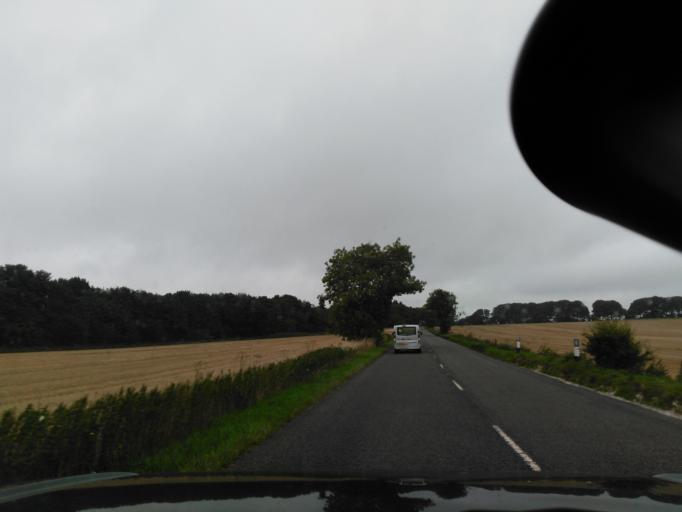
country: GB
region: England
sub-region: Wiltshire
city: Chicklade
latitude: 51.1102
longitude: -2.1690
